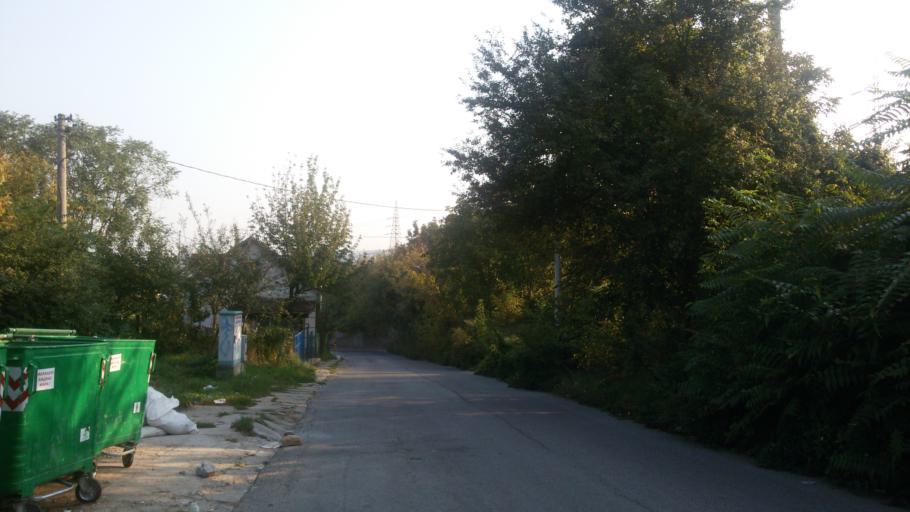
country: RS
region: Central Serbia
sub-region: Belgrade
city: Cukarica
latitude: 44.7483
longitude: 20.3997
